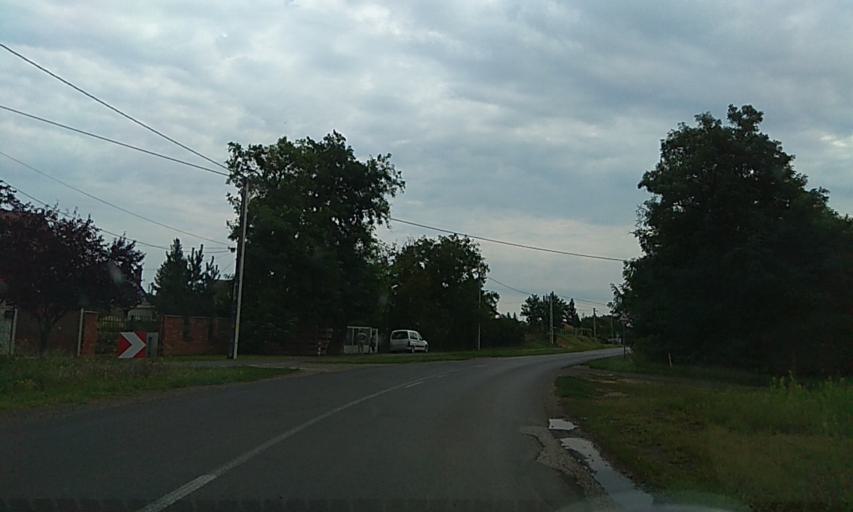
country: HU
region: Szabolcs-Szatmar-Bereg
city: Kotaj
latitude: 48.0054
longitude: 21.6976
